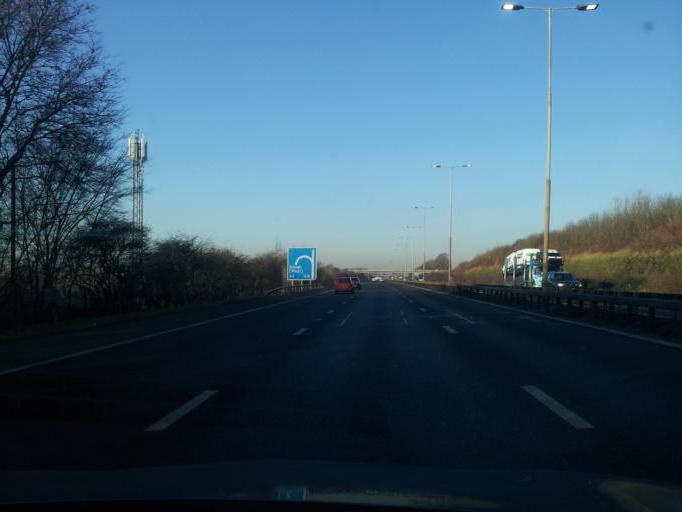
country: GB
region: England
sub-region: West Berkshire
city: Eton
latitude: 51.5088
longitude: -0.6427
